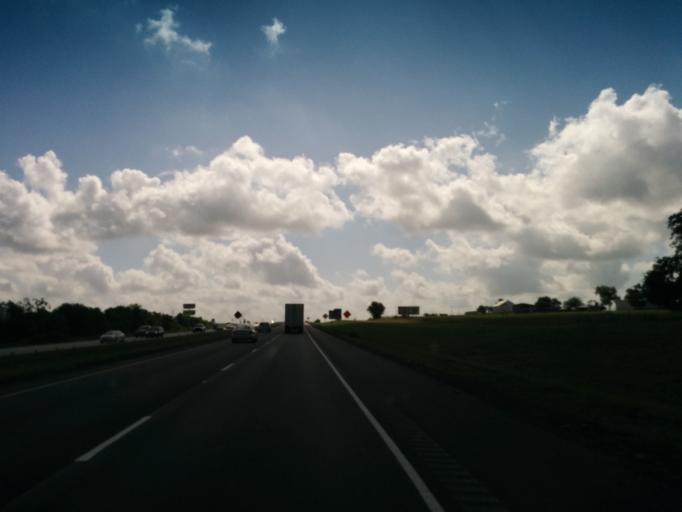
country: US
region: Texas
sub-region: Colorado County
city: Weimar
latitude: 29.6907
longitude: -96.7897
